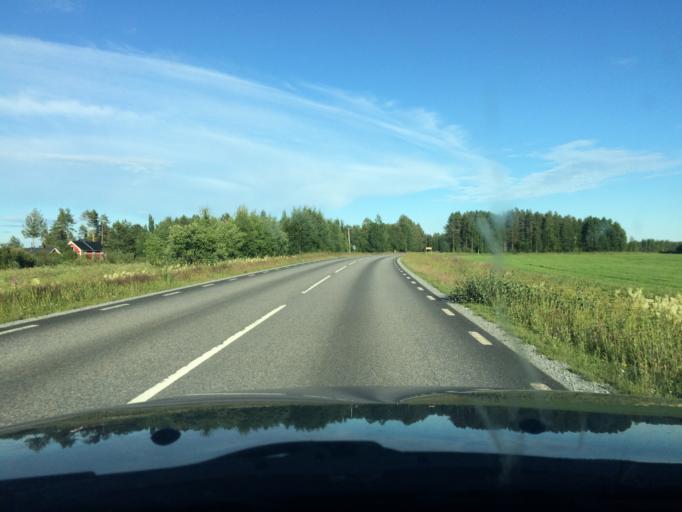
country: SE
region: Norrbotten
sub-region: Pitea Kommun
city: Roknas
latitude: 65.3380
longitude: 21.1853
